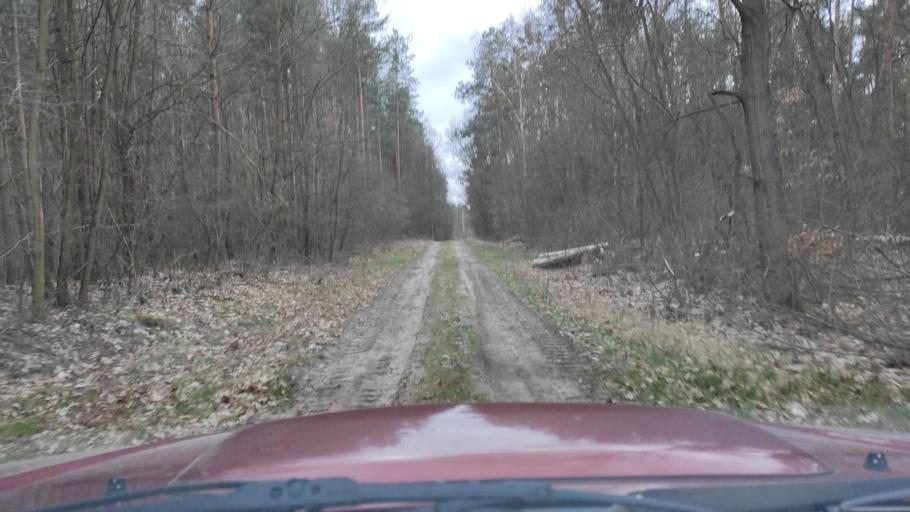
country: PL
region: Masovian Voivodeship
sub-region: Powiat kozienicki
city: Garbatka-Letnisko
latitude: 51.5095
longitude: 21.5474
